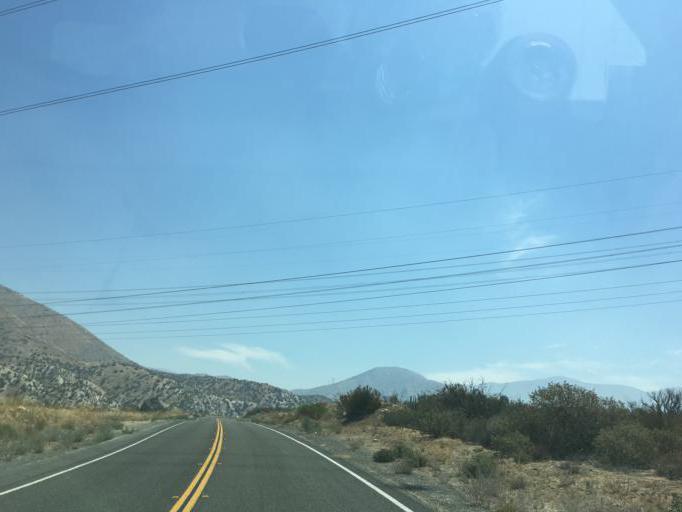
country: US
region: California
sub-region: Los Angeles County
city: Vincent
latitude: 34.4359
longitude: -118.1351
